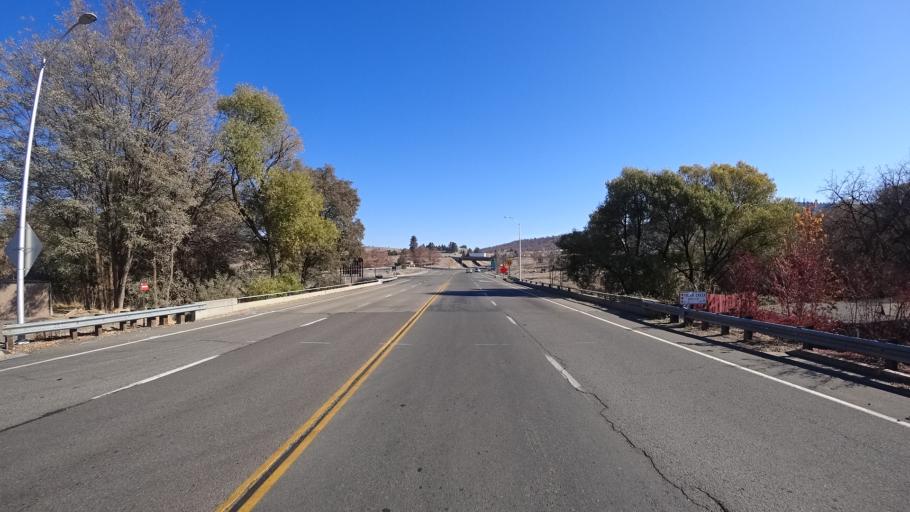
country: US
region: California
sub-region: Siskiyou County
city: Yreka
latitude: 41.7401
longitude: -122.6312
